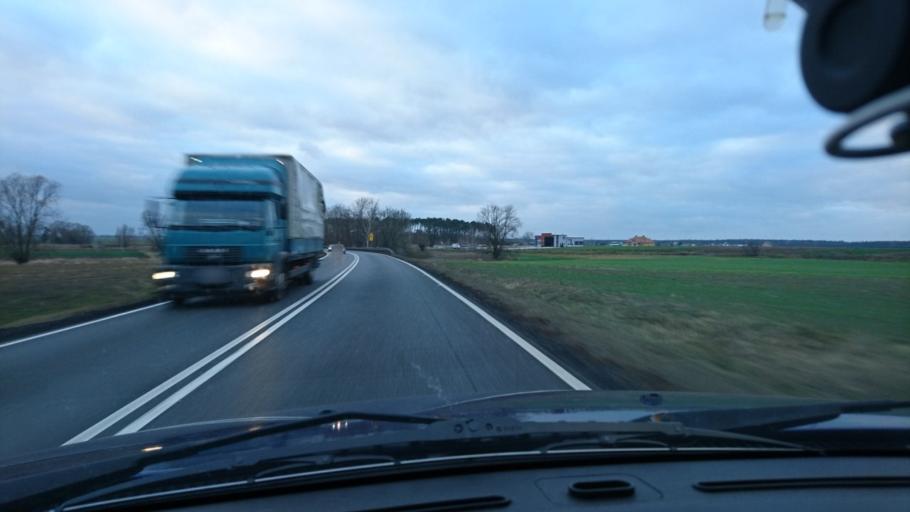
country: PL
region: Greater Poland Voivodeship
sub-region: Powiat kepinski
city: Opatow
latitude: 51.2206
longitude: 18.1342
